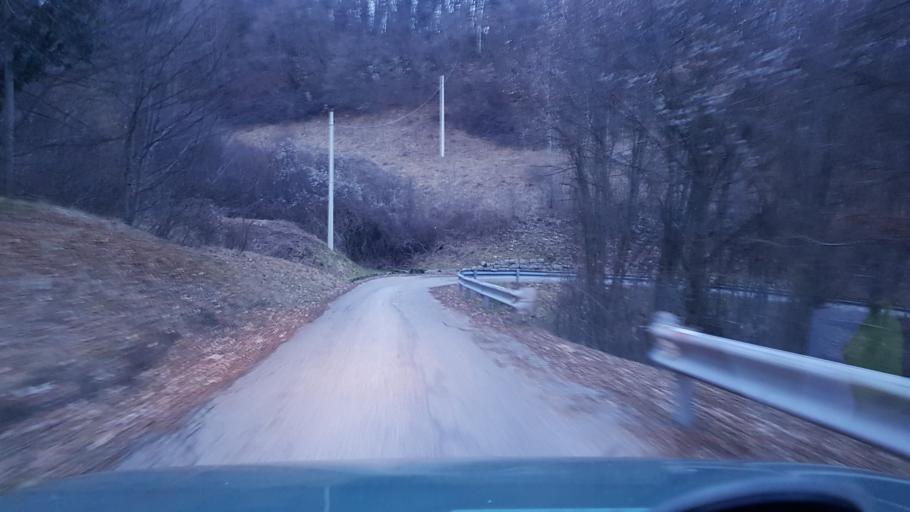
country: IT
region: Friuli Venezia Giulia
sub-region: Provincia di Udine
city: Pulfero
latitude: 46.1458
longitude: 13.4622
